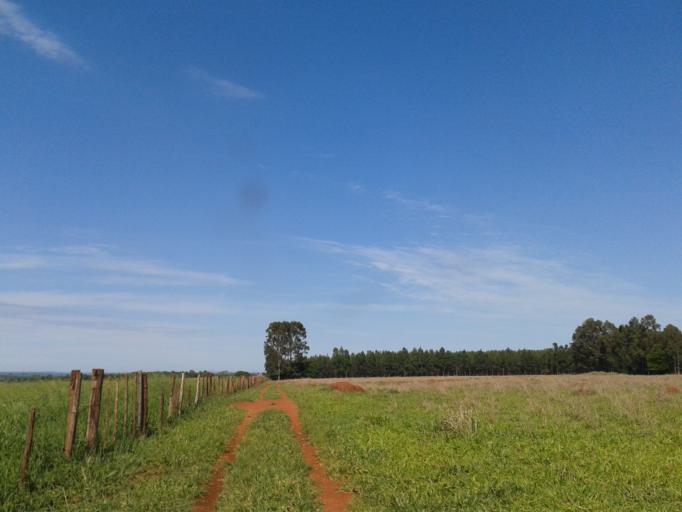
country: BR
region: Minas Gerais
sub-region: Centralina
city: Centralina
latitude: -18.7201
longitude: -49.1629
